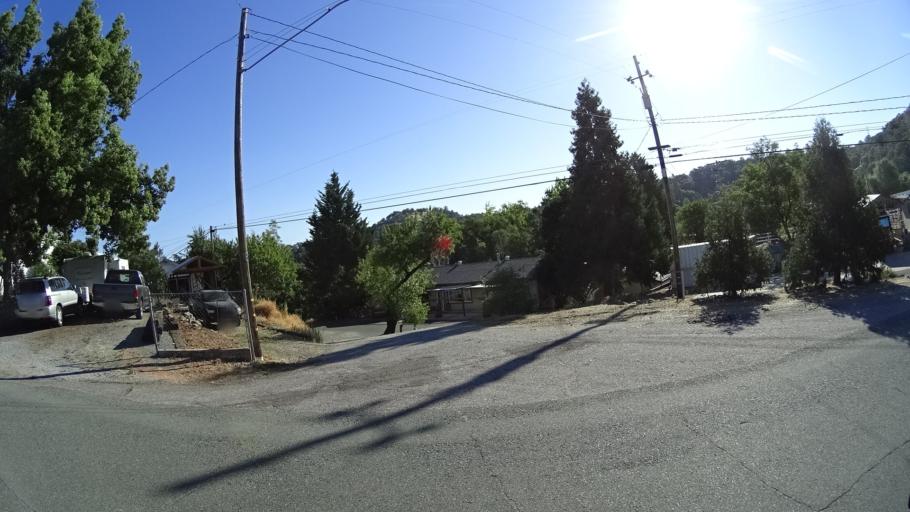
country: US
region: California
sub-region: Amador County
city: Jackson
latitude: 38.2990
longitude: -120.7036
